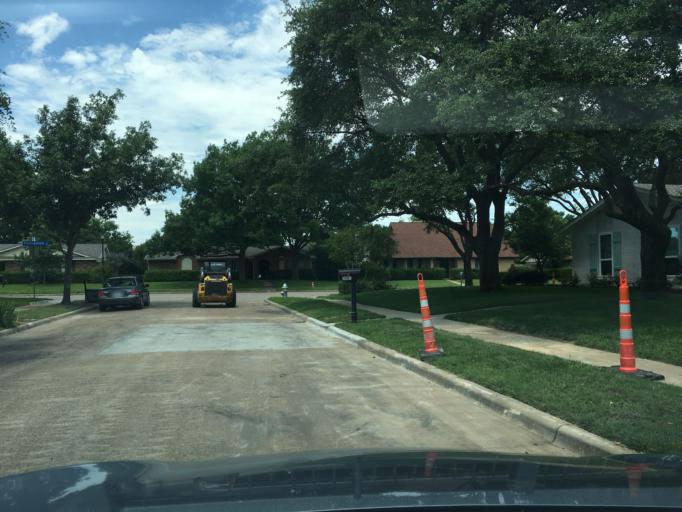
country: US
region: Texas
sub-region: Dallas County
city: Richardson
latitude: 32.9372
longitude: -96.6855
